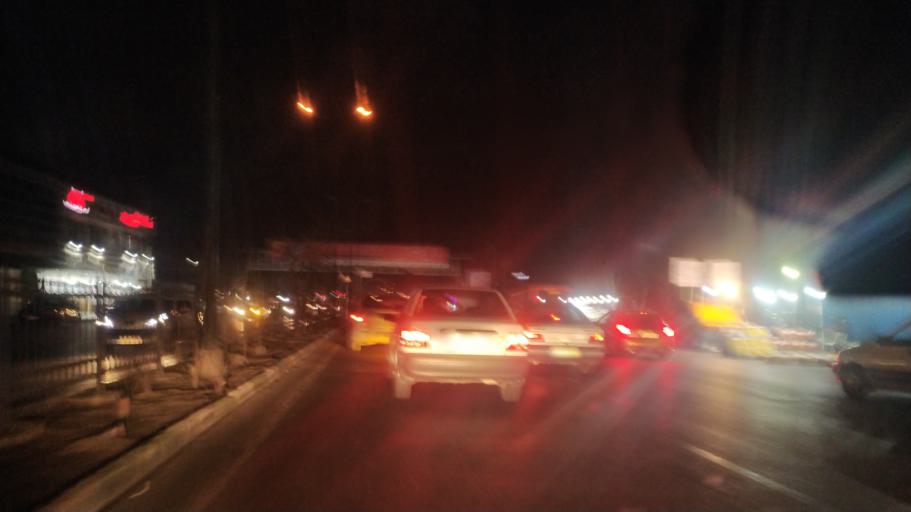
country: IR
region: Alborz
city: Karaj
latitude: 35.7803
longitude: 51.0061
